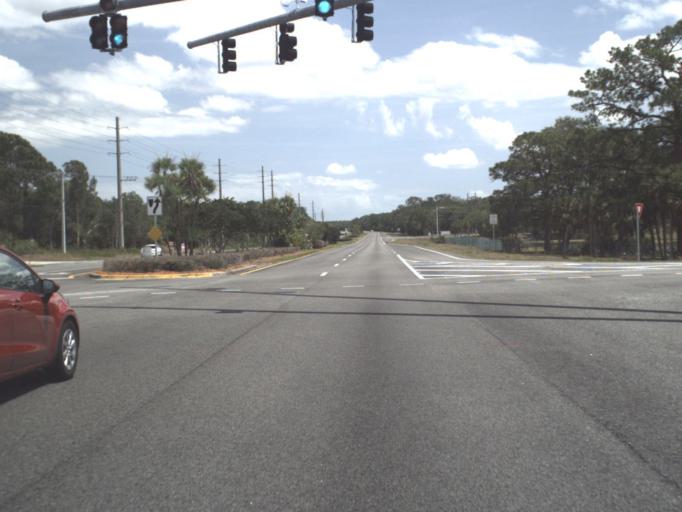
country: US
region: Florida
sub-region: Brevard County
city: Port Saint John
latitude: 28.5302
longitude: -80.8106
